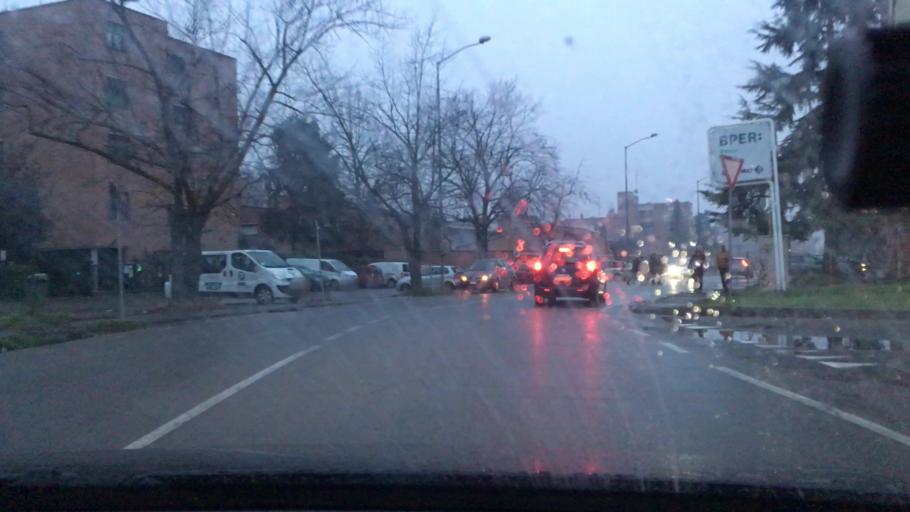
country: IT
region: Emilia-Romagna
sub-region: Provincia di Modena
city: Modena
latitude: 44.6395
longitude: 10.8885
